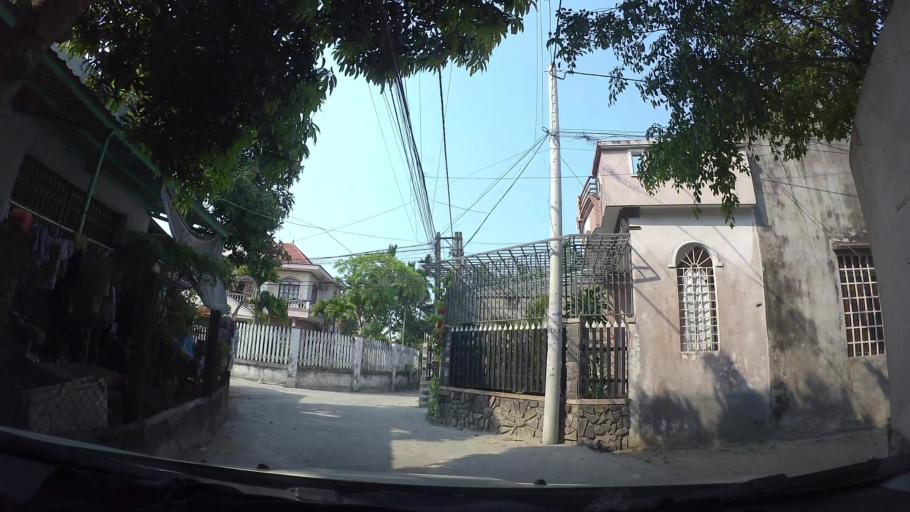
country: VN
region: Da Nang
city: Cam Le
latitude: 16.0031
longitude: 108.1932
